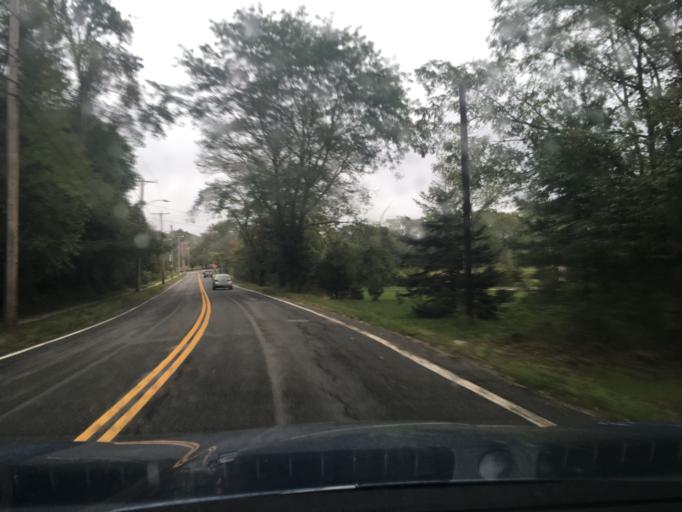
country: US
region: Rhode Island
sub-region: Washington County
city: North Kingstown
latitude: 41.5664
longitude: -71.4595
